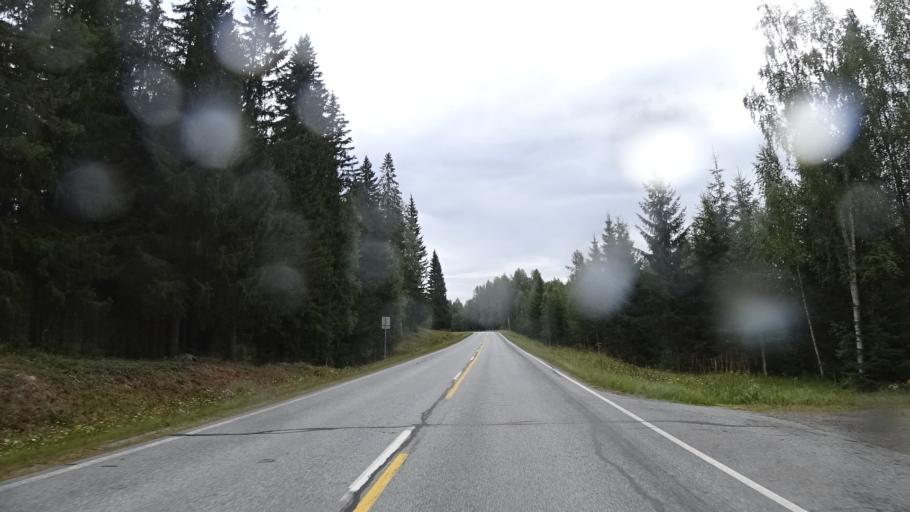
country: FI
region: North Karelia
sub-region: Keski-Karjala
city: Raeaekkylae
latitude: 62.1068
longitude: 29.6978
